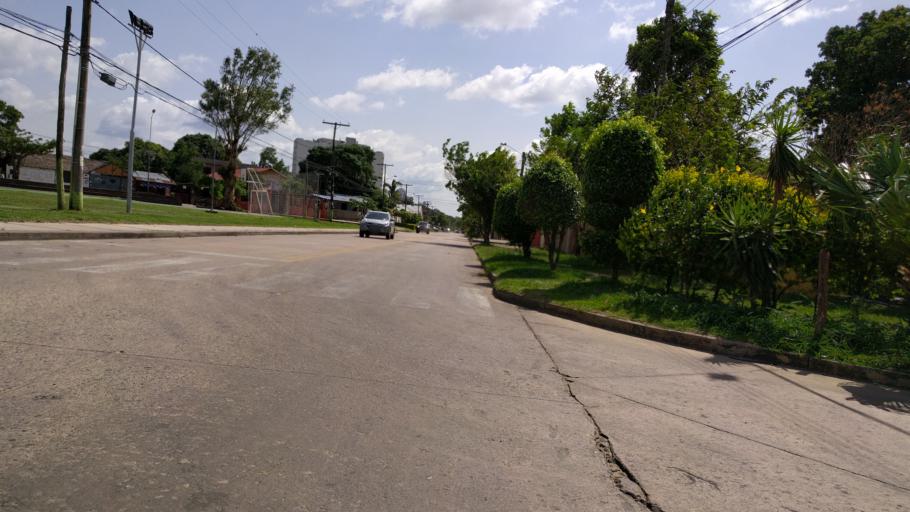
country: BO
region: Santa Cruz
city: Santa Cruz de la Sierra
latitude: -17.7746
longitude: -63.2118
